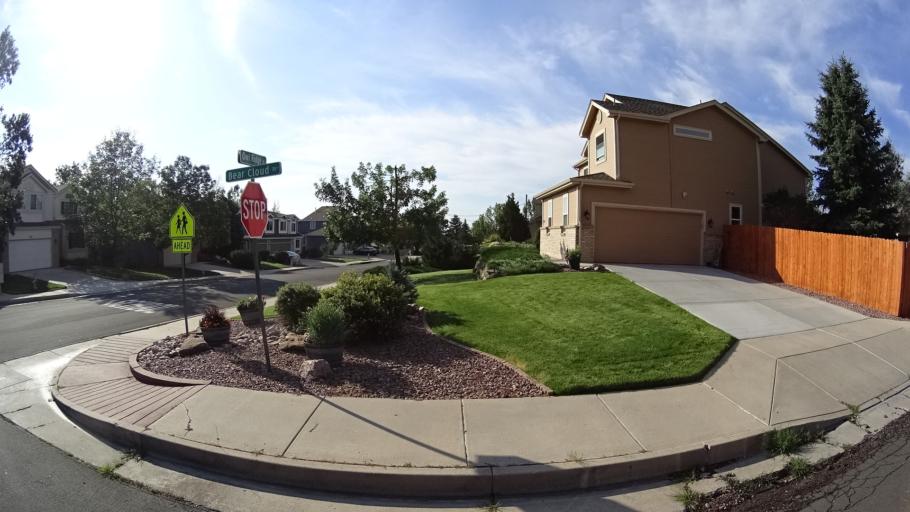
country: US
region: Colorado
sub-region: El Paso County
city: Air Force Academy
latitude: 38.9244
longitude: -104.8517
